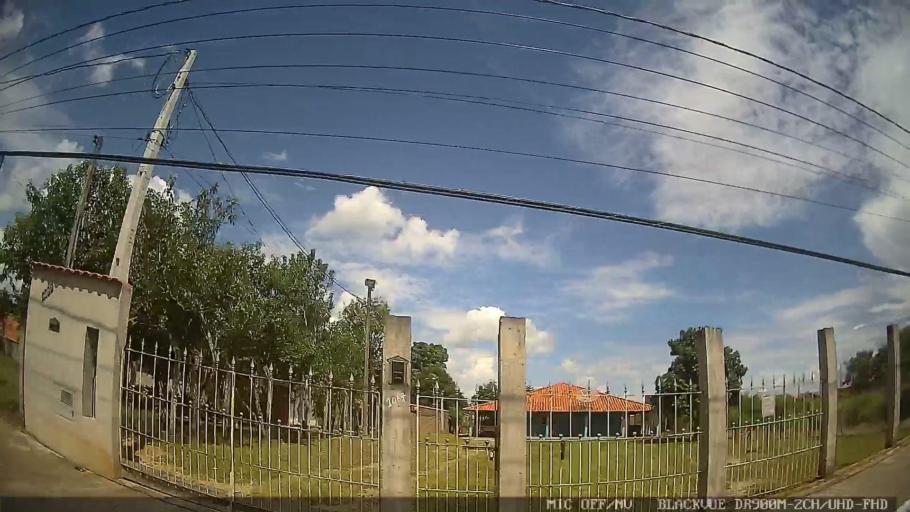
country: BR
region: Sao Paulo
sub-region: Conchas
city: Conchas
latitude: -23.0379
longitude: -48.0185
